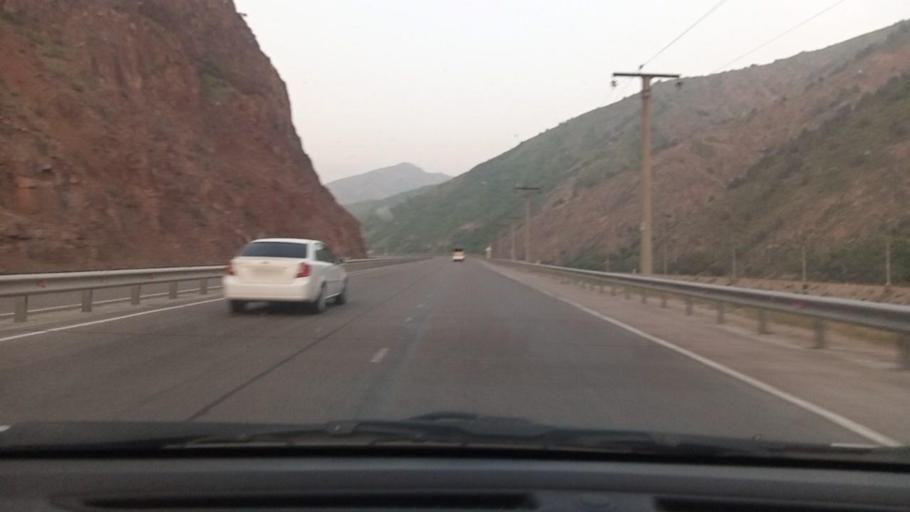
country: UZ
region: Toshkent
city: Angren
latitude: 41.1403
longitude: 70.3965
